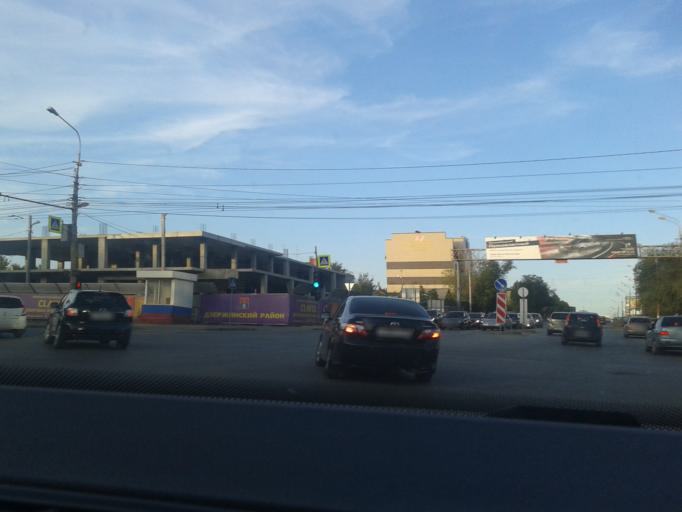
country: RU
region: Volgograd
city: Volgograd
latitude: 48.7192
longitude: 44.5063
